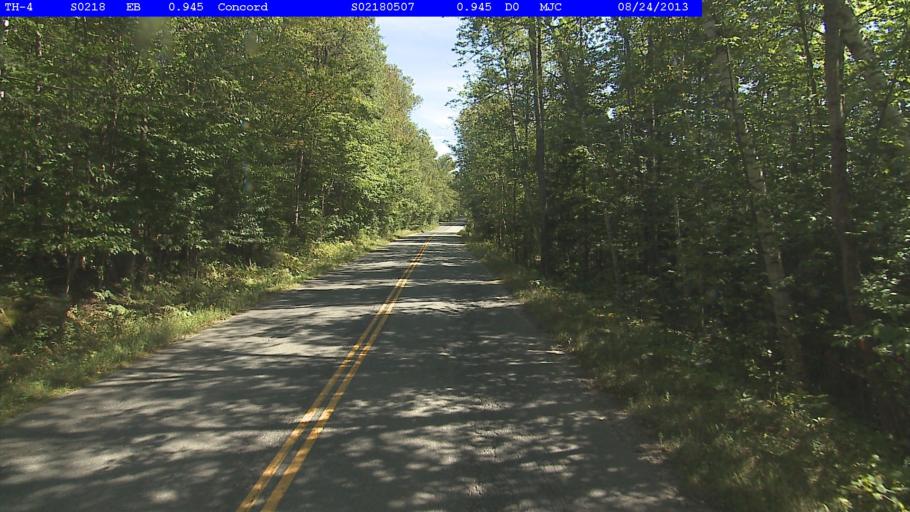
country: US
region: New Hampshire
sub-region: Grafton County
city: Littleton
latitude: 44.4521
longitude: -71.7692
